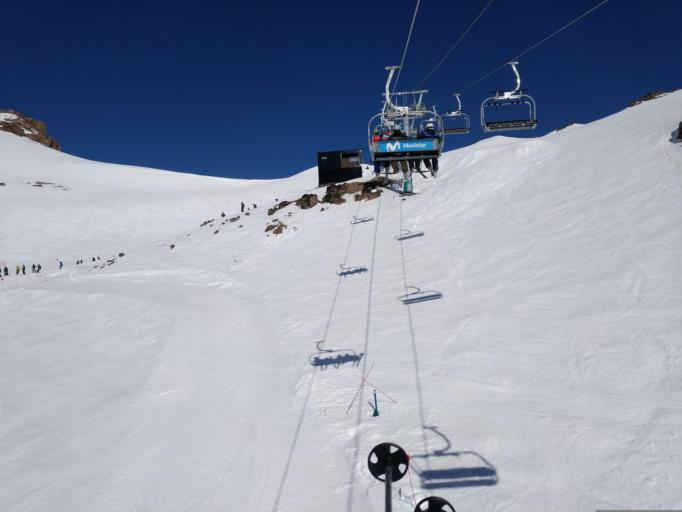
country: AR
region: Rio Negro
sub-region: Departamento de Bariloche
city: San Carlos de Bariloche
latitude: -41.1729
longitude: -71.4834
